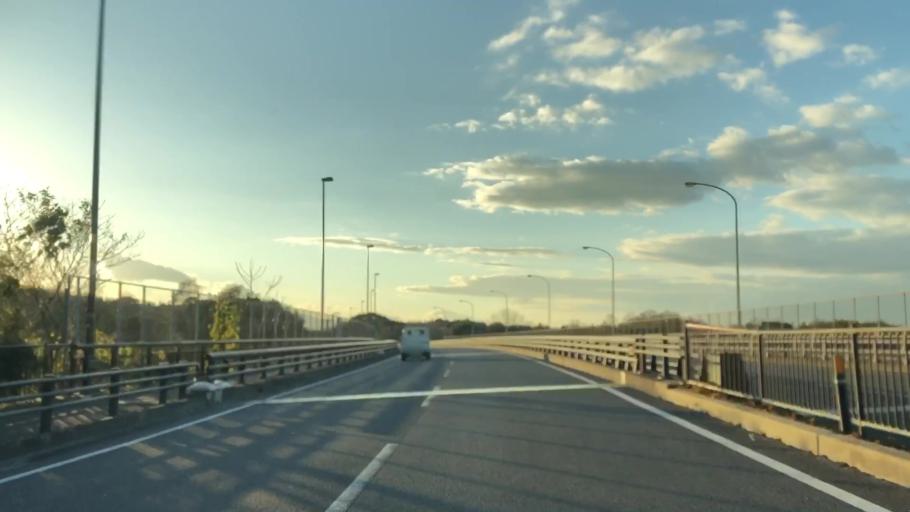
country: JP
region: Fukuoka
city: Nakatsu
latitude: 33.5542
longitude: 131.2536
